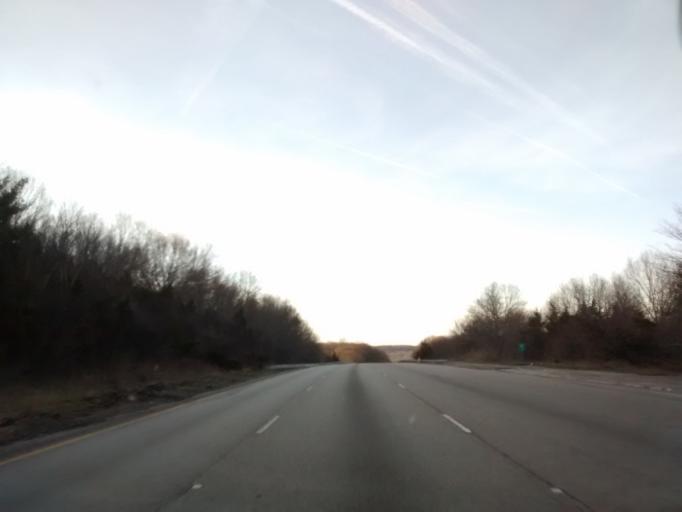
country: US
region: Massachusetts
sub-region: Worcester County
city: Southborough
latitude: 42.2932
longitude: -71.5661
